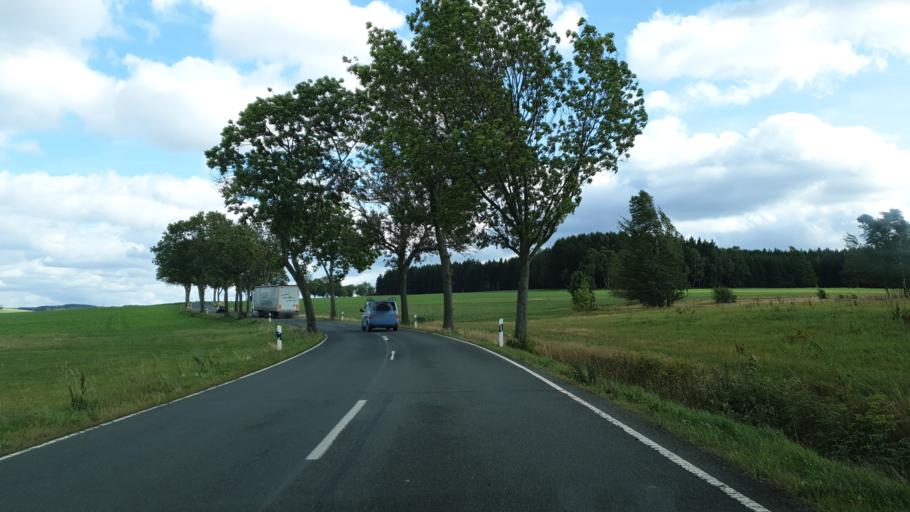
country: DE
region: Saxony
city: Lossnitz
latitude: 50.6534
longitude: 12.7124
